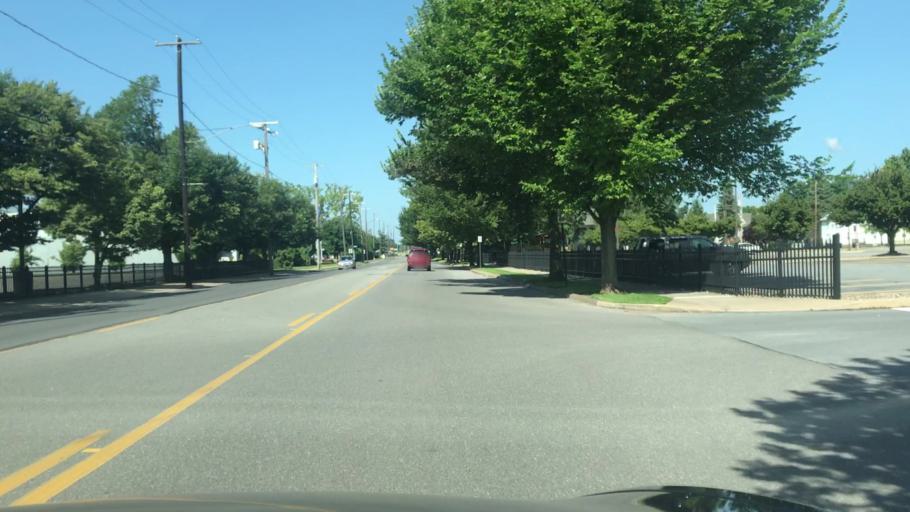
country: US
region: Pennsylvania
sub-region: Lycoming County
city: Duboistown
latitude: 41.2374
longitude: -77.0270
